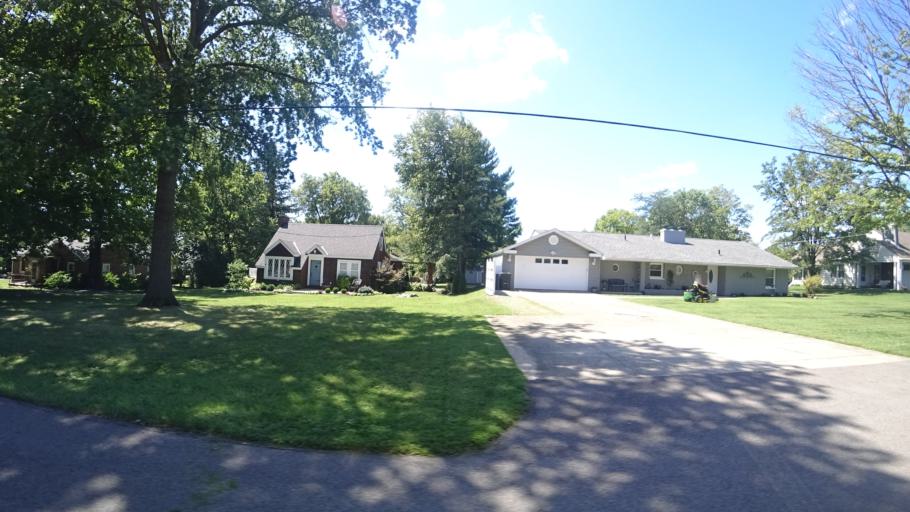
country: US
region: Ohio
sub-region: Butler County
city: New Miami
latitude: 39.4063
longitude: -84.5281
